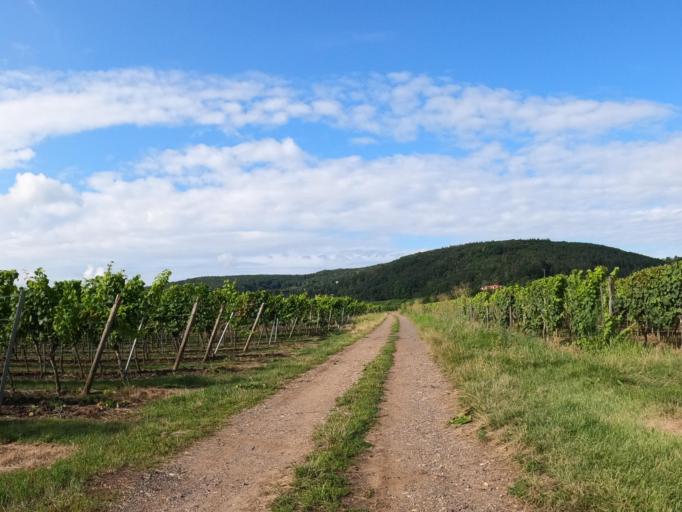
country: DE
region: Rheinland-Pfalz
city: Kleinkarlbach
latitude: 49.5324
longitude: 8.1551
